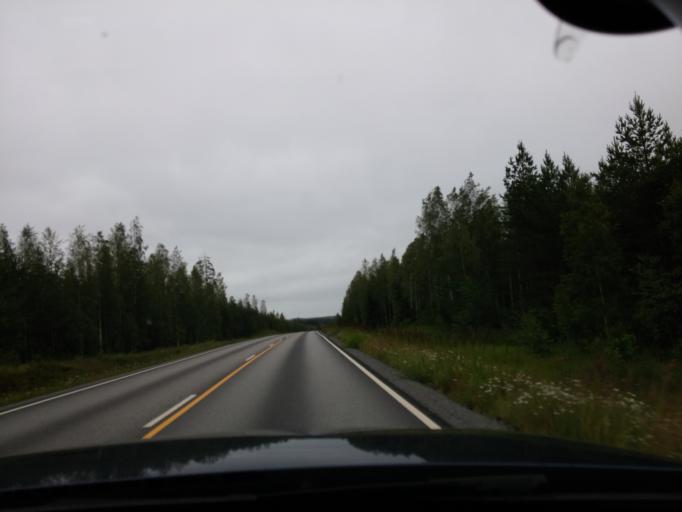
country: FI
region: Central Finland
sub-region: Saarijaervi-Viitasaari
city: Saarijaervi
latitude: 62.6795
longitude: 25.1894
